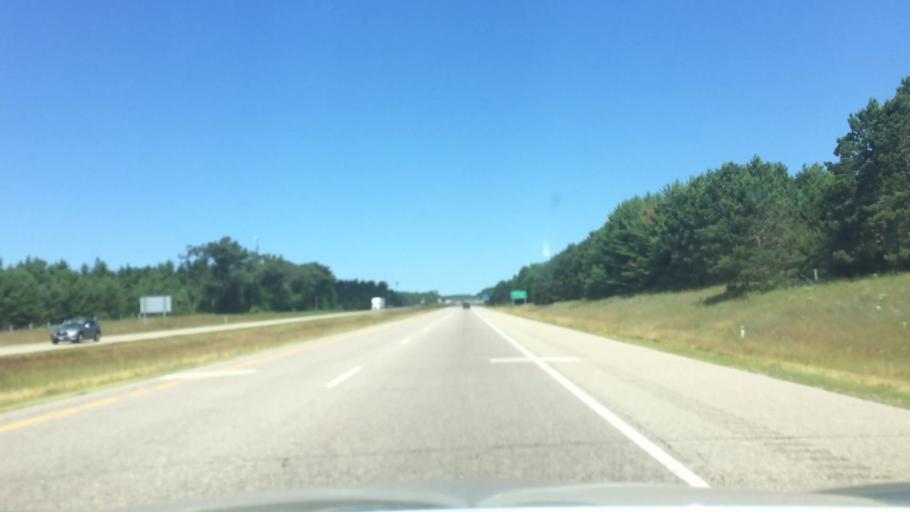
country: US
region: Wisconsin
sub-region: Marquette County
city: Westfield
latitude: 44.0230
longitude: -89.5174
